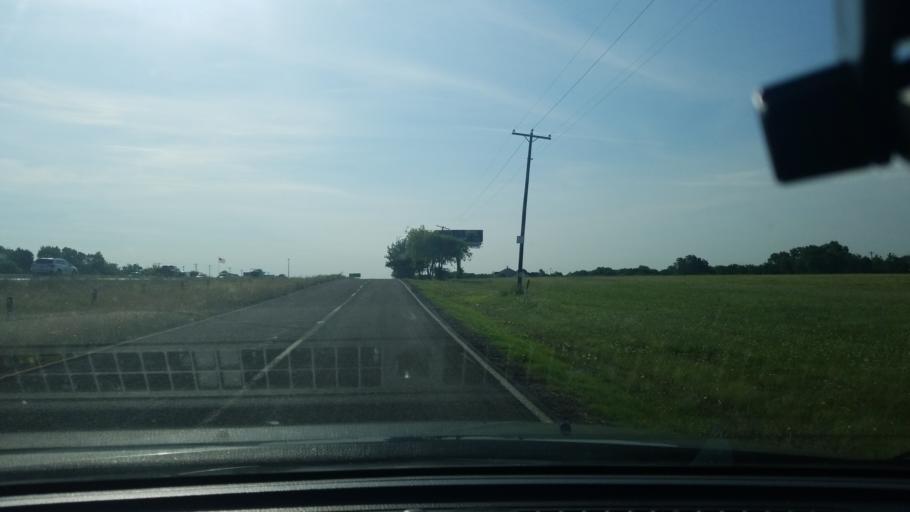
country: US
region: Texas
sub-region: Dallas County
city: Sunnyvale
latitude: 32.7833
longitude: -96.5543
